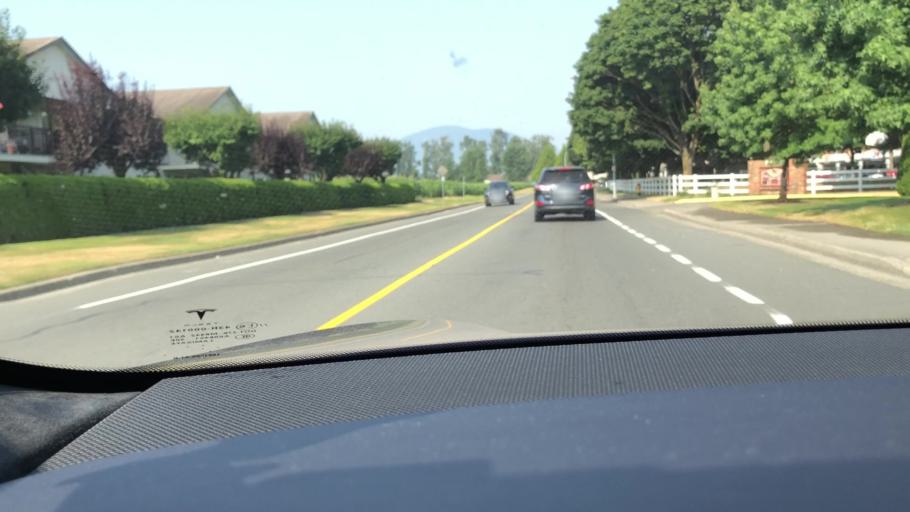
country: CA
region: British Columbia
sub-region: Fraser Valley Regional District
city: Chilliwack
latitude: 49.1381
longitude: -121.9612
